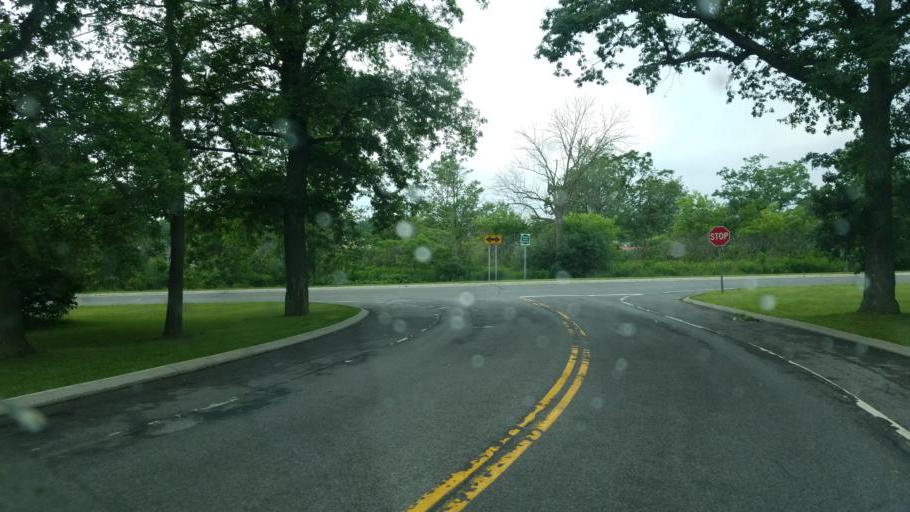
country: CA
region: Ontario
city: Niagara Falls
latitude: 43.1162
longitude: -79.0593
